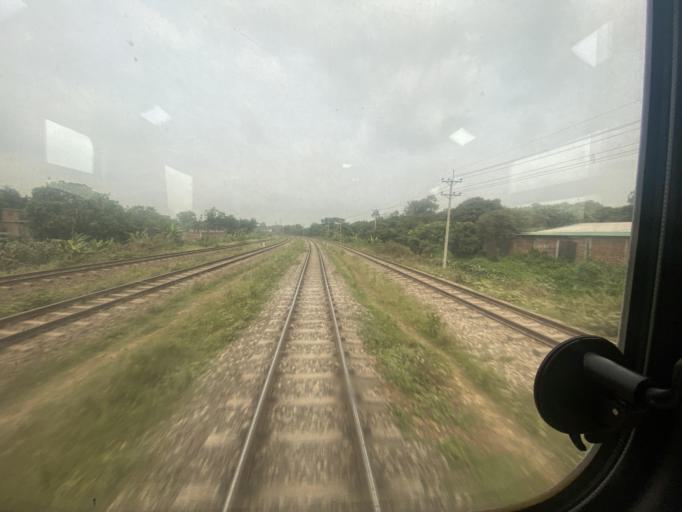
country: BD
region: Dhaka
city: Tungi
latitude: 23.9364
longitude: 90.4748
